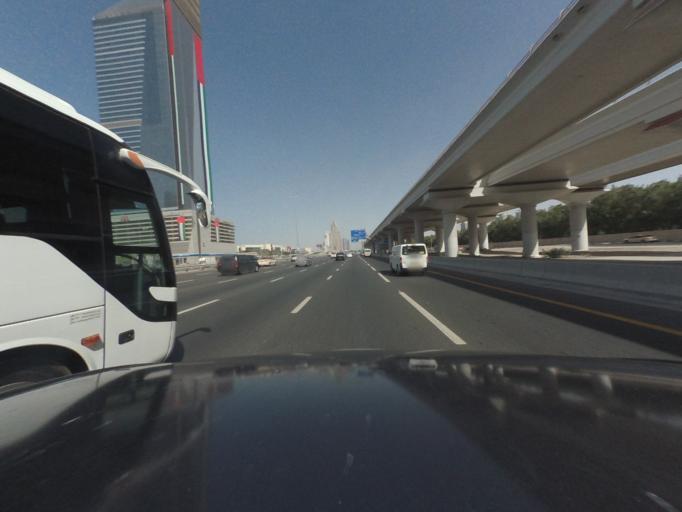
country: AE
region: Dubai
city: Dubai
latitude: 25.0896
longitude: 55.1588
